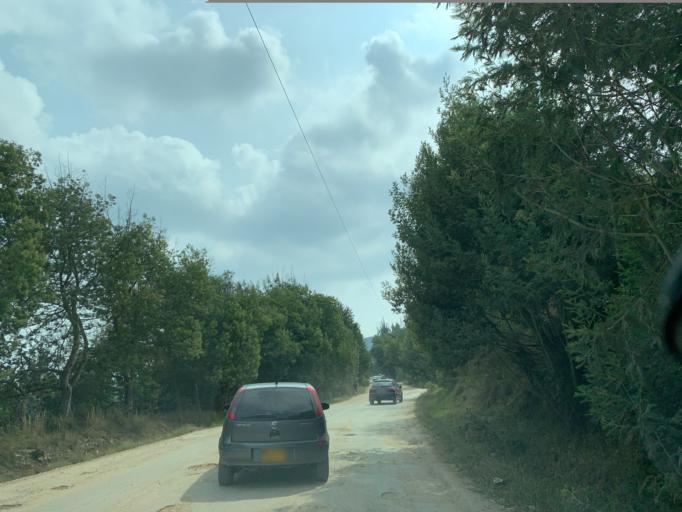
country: CO
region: Boyaca
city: Siachoque
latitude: 5.5510
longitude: -73.2938
